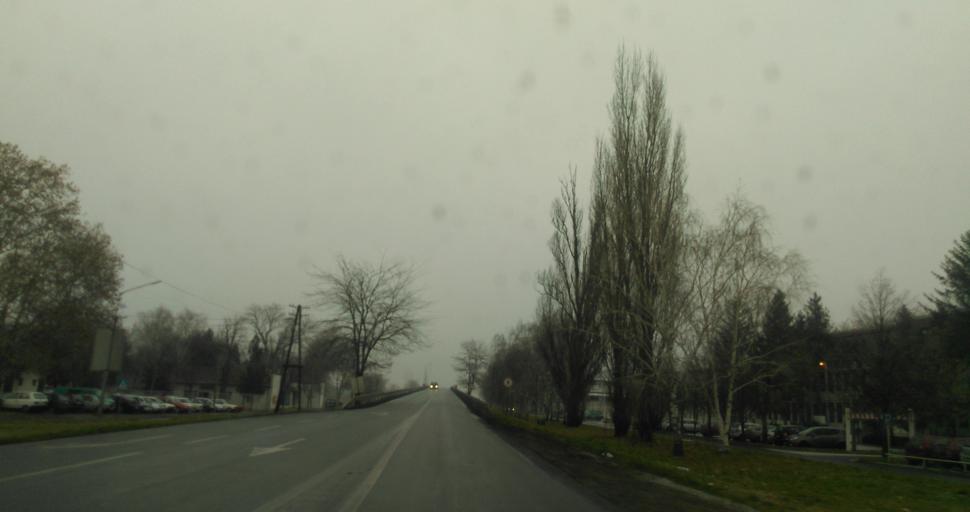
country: RS
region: Autonomna Pokrajina Vojvodina
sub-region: Srednjebanatski Okrug
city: Zrenjanin
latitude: 45.3725
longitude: 20.4157
